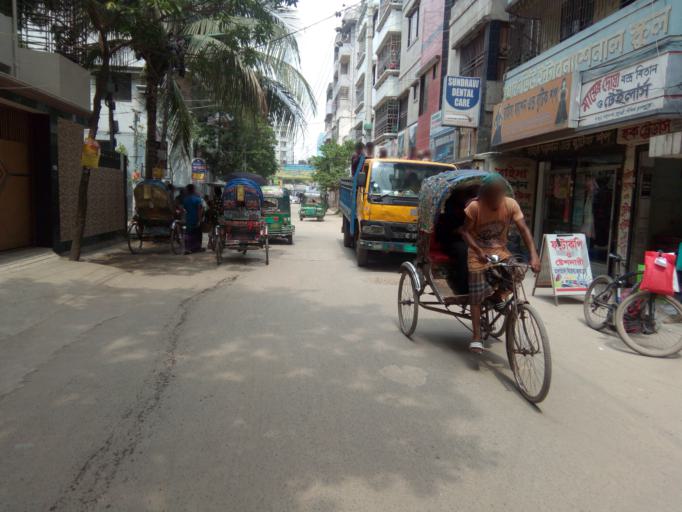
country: BD
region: Dhaka
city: Paltan
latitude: 23.7635
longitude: 90.4149
